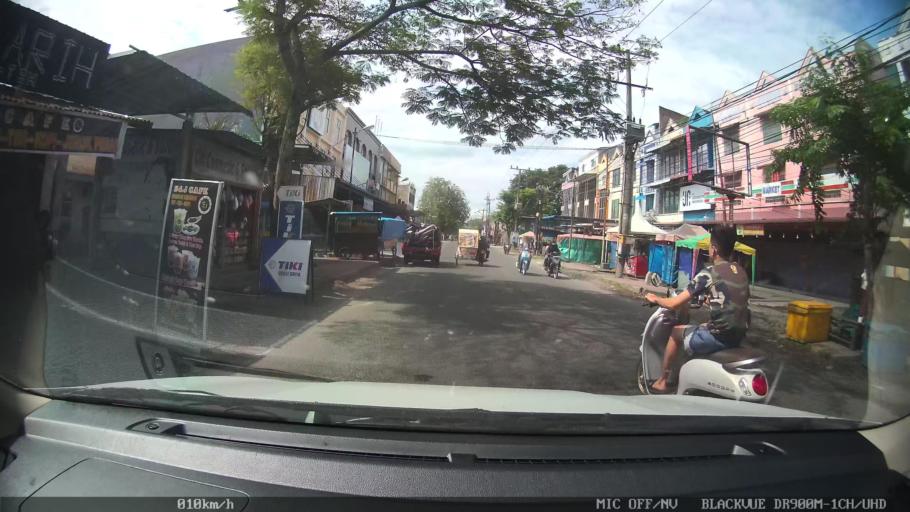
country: ID
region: North Sumatra
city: Medan
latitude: 3.6072
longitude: 98.6450
